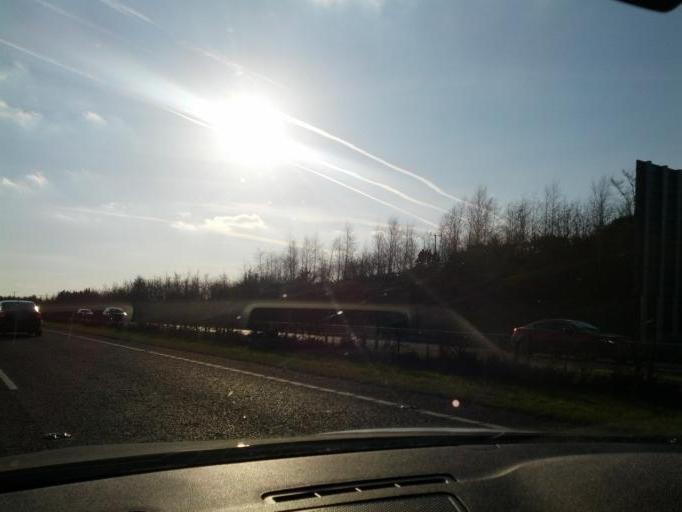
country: IE
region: Leinster
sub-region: Laois
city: Stradbally
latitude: 53.0775
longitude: -7.2001
